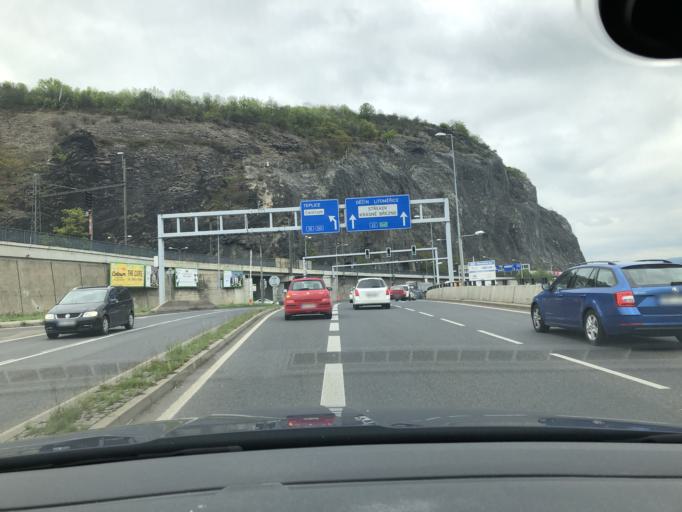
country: CZ
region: Ustecky
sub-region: Okres Usti nad Labem
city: Usti nad Labem
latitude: 50.6601
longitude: 14.0470
